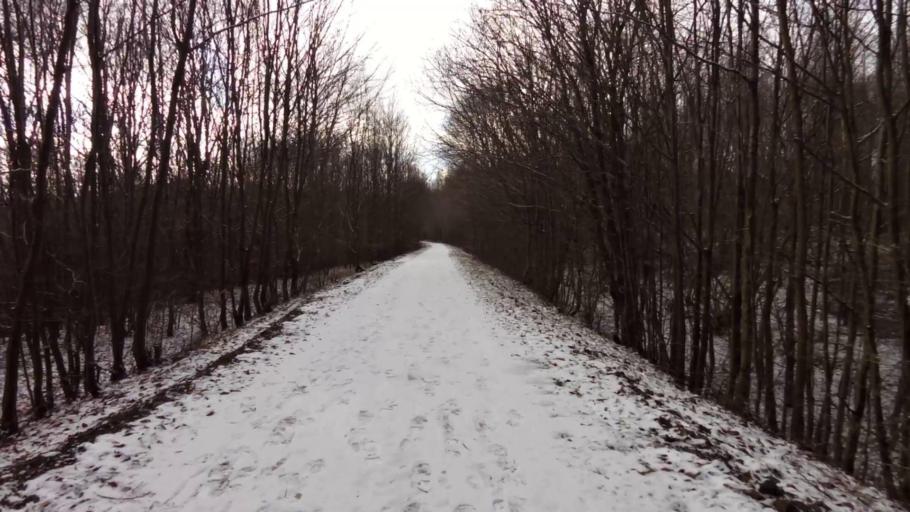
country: PL
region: West Pomeranian Voivodeship
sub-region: Powiat swidwinski
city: Polczyn-Zdroj
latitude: 53.7453
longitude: 16.0602
